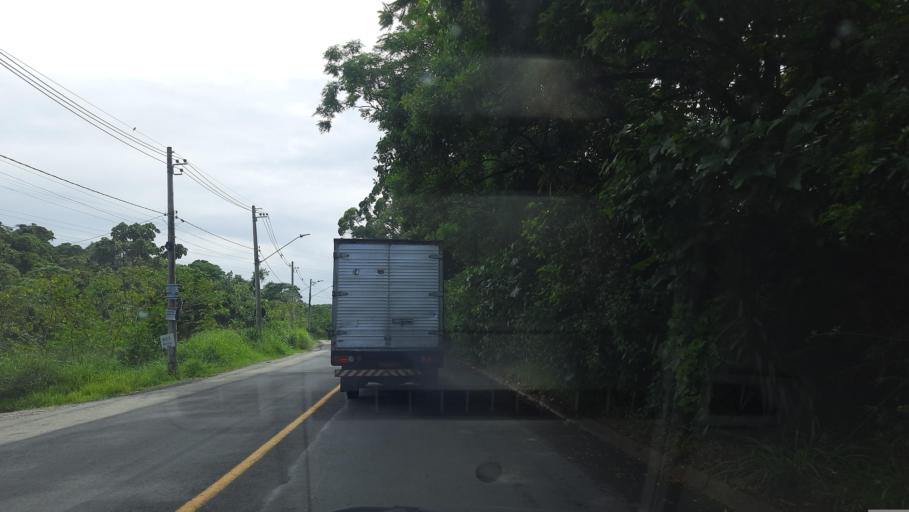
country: BR
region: Sao Paulo
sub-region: Caieiras
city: Caieiras
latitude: -23.3661
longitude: -46.6741
